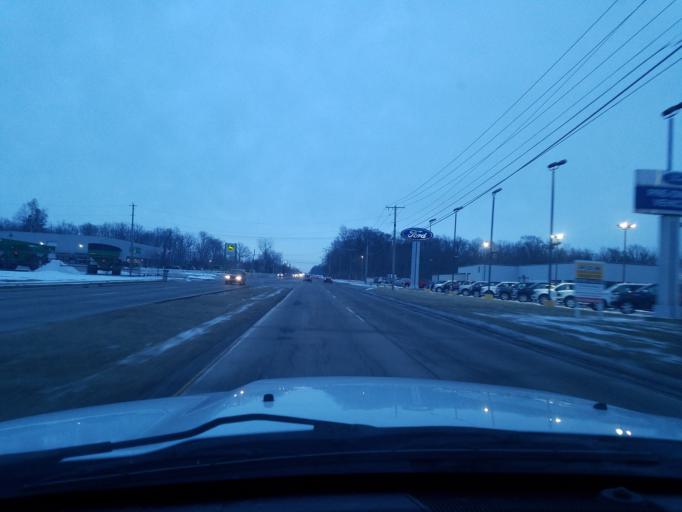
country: US
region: Indiana
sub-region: Delaware County
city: Muncie
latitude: 40.2190
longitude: -85.3644
